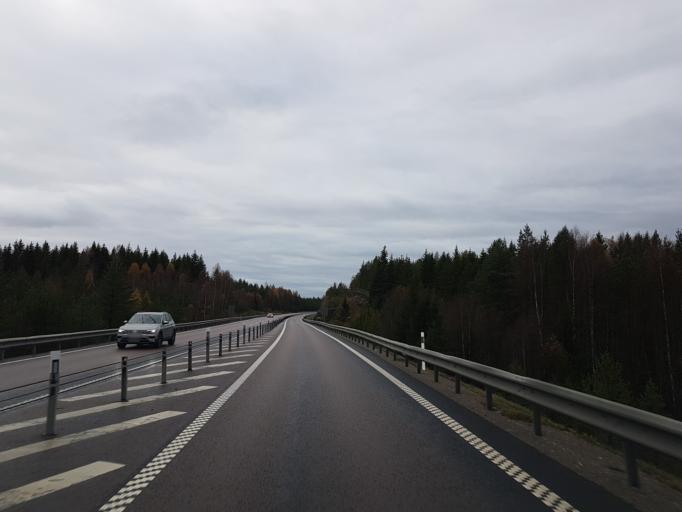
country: SE
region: Gaevleborg
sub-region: Hudiksvalls Kommun
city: Hudiksvall
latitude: 61.7853
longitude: 17.1356
